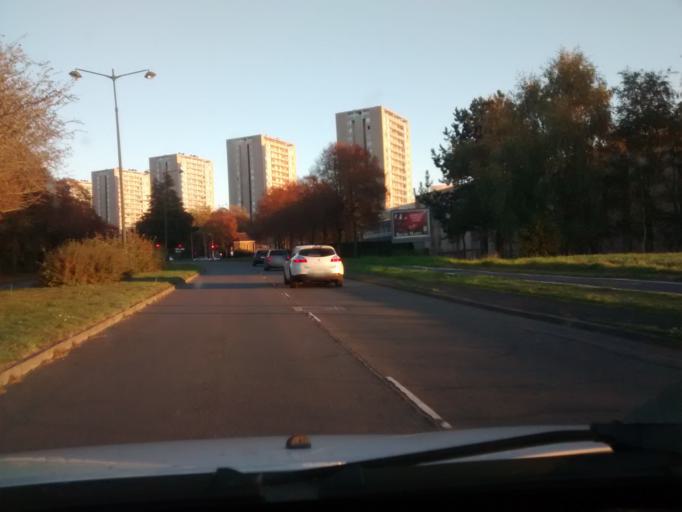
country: FR
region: Brittany
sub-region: Departement d'Ille-et-Vilaine
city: Rennes
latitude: 48.1292
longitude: -1.6664
